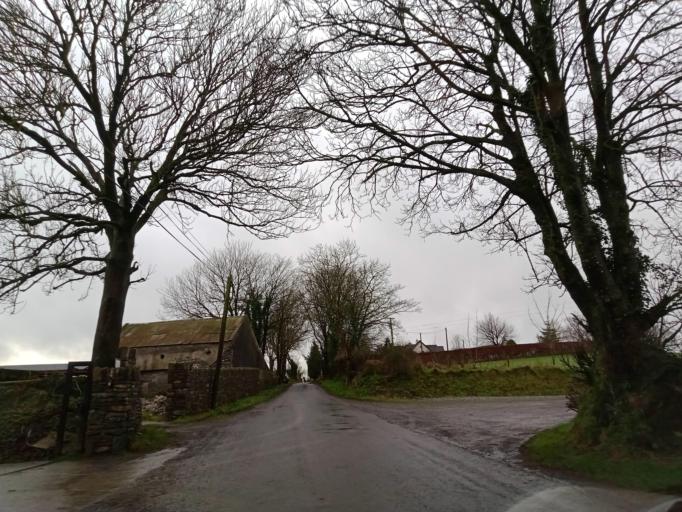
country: IE
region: Munster
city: Fethard
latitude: 52.5625
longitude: -7.6902
